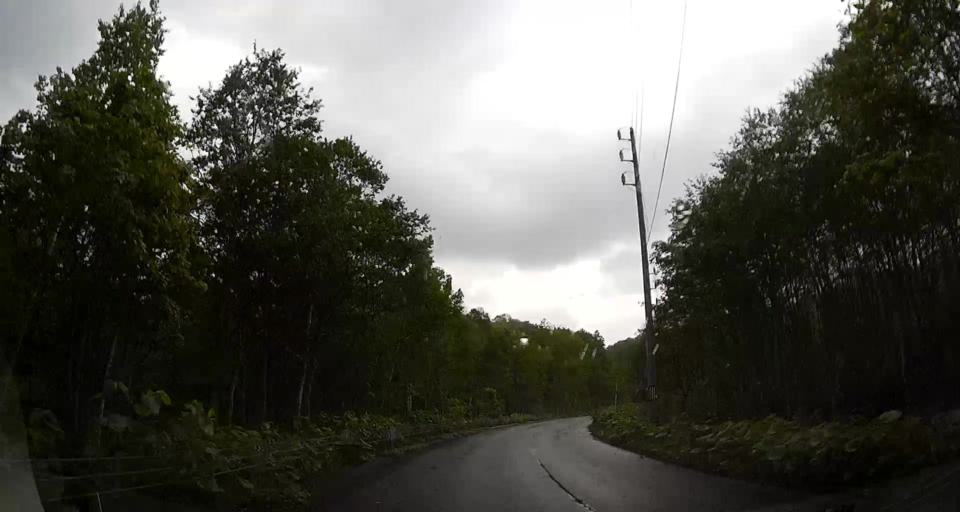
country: JP
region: Hokkaido
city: Otaru
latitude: 42.9153
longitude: 140.9271
